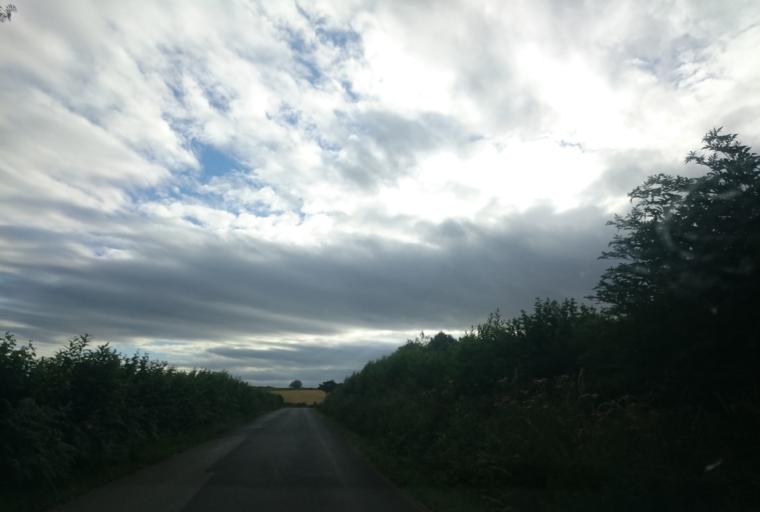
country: FR
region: Auvergne
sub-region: Departement du Cantal
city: Sansac-de-Marmiesse
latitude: 44.8090
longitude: 2.3963
